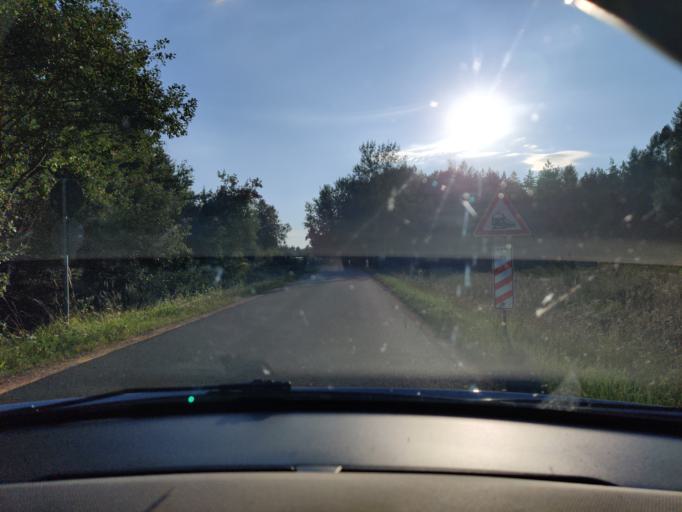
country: DE
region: Bavaria
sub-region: Upper Palatinate
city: Stulln
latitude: 49.4262
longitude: 12.1608
